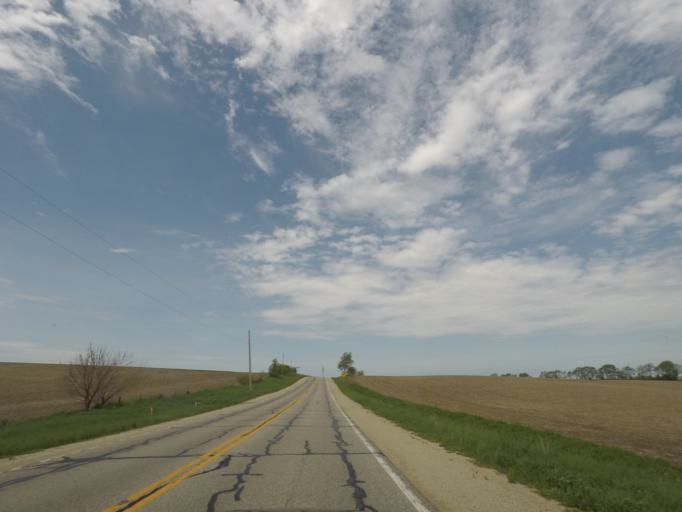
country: US
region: Wisconsin
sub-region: Rock County
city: Orfordville
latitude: 42.6068
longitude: -89.2264
